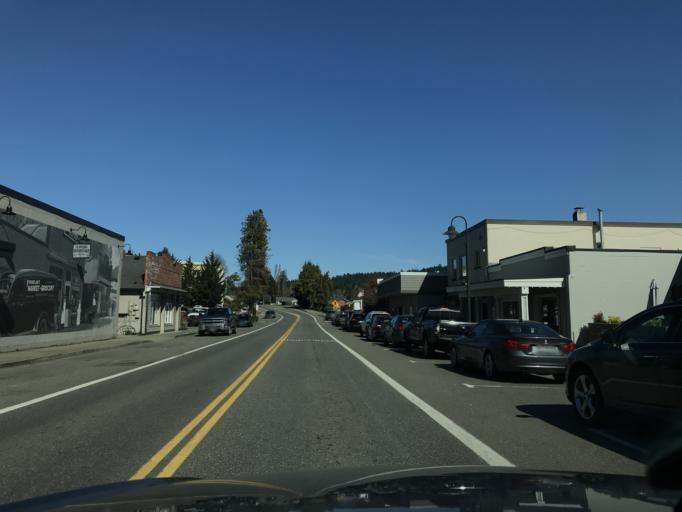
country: US
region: Washington
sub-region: Pierce County
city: Gig Harbor
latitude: 47.3387
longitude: -122.5907
